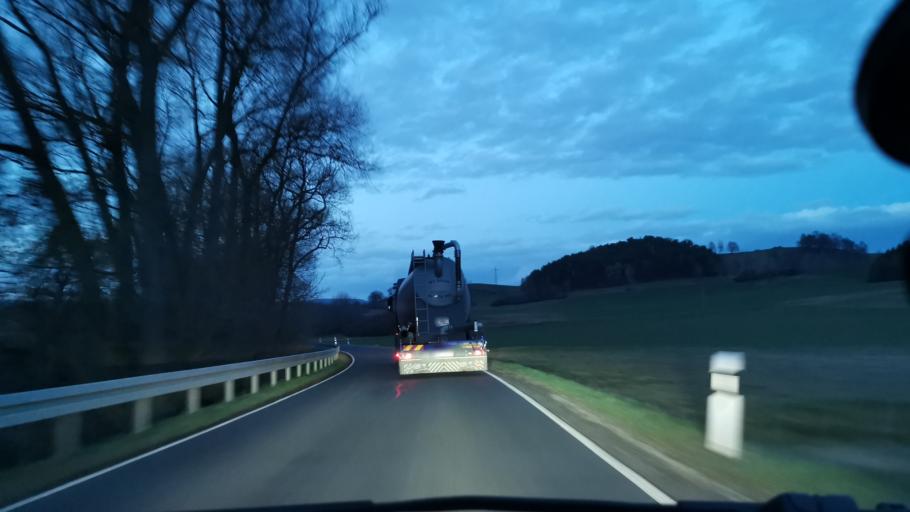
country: DE
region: Hesse
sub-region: Regierungsbezirk Kassel
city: Cornberg
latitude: 51.0987
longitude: 9.8131
